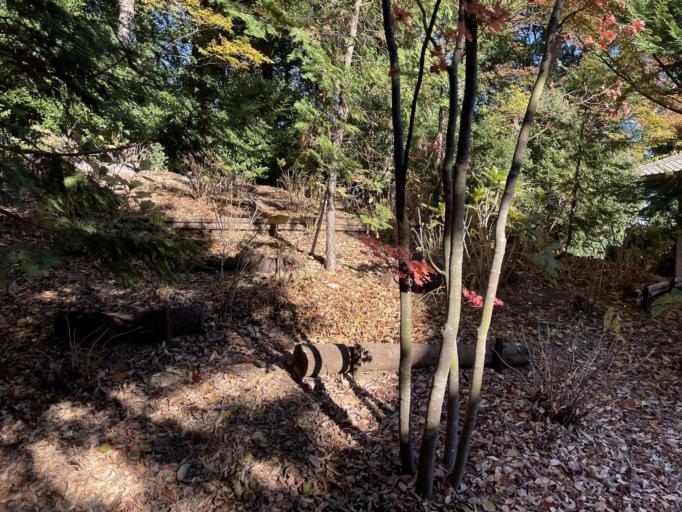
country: JP
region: Saitama
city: Wako
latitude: 35.7919
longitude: 139.6344
